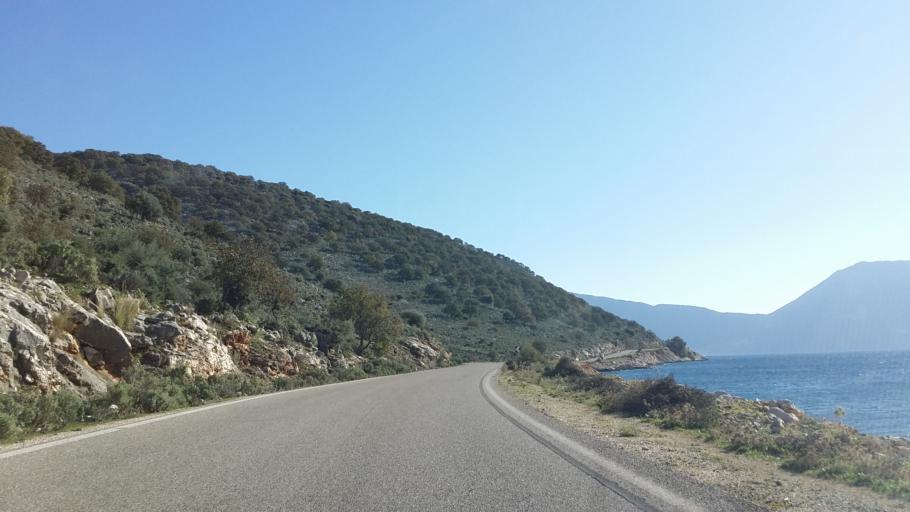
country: GR
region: West Greece
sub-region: Nomos Aitolias kai Akarnanias
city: Kandila
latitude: 38.7061
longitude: 20.8956
